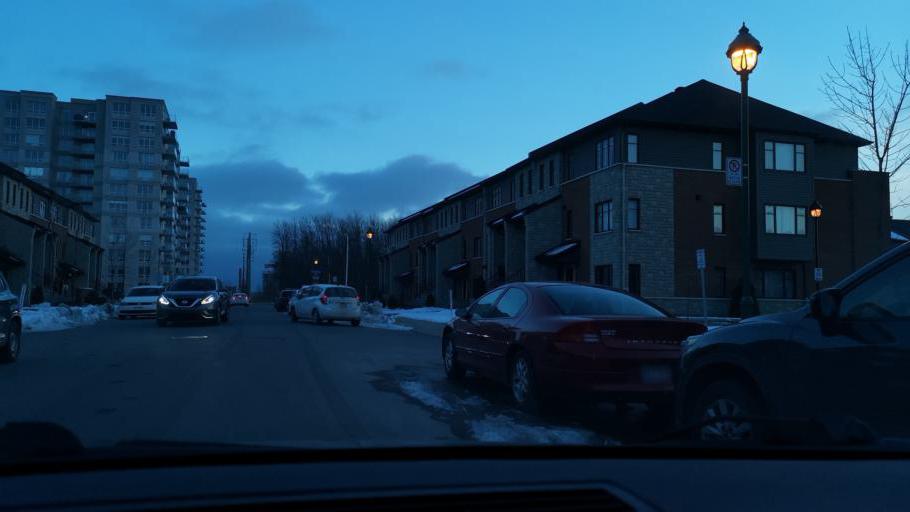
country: CA
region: Quebec
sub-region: Laurentides
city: Rosemere
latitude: 45.5718
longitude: -73.7711
